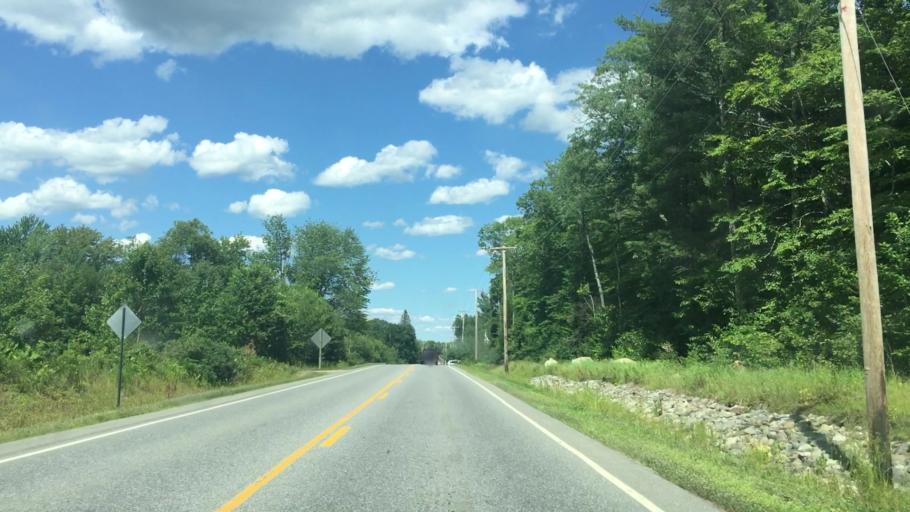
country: US
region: Maine
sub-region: Franklin County
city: Chesterville
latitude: 44.6162
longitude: -70.0798
